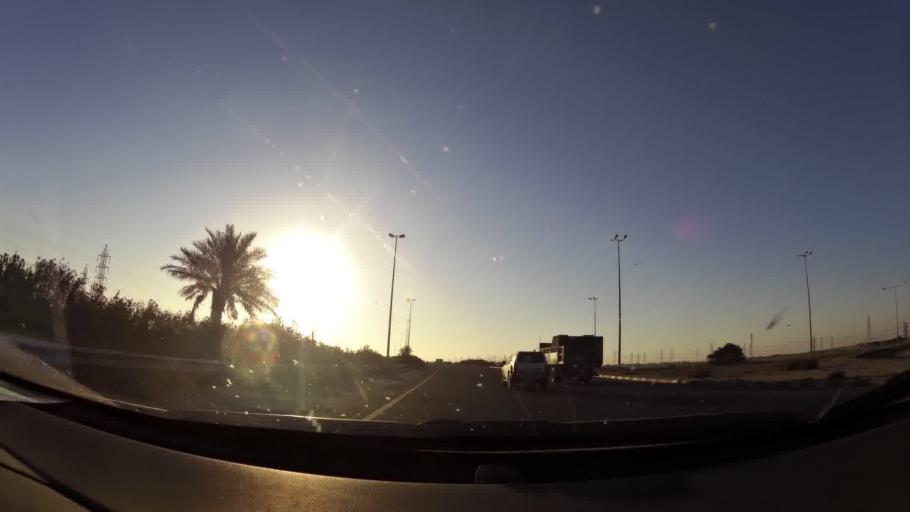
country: KW
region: Al Ahmadi
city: Al Fahahil
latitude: 28.9401
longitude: 48.1846
